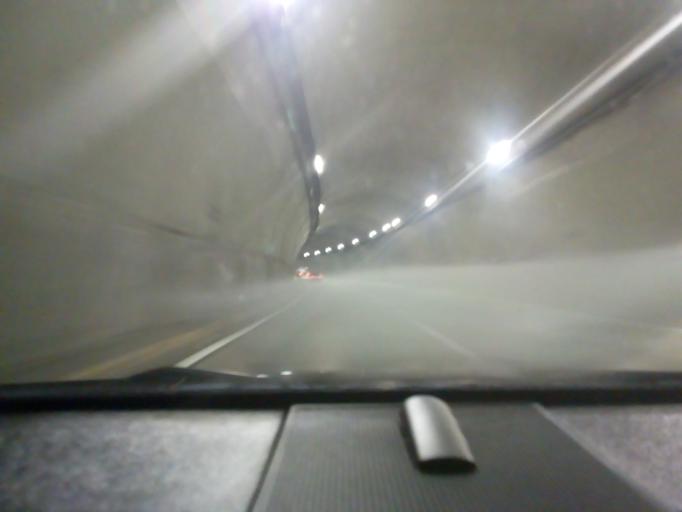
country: BR
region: Sao Paulo
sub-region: Jacarei
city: Jacarei
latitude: -23.3443
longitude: -45.9874
